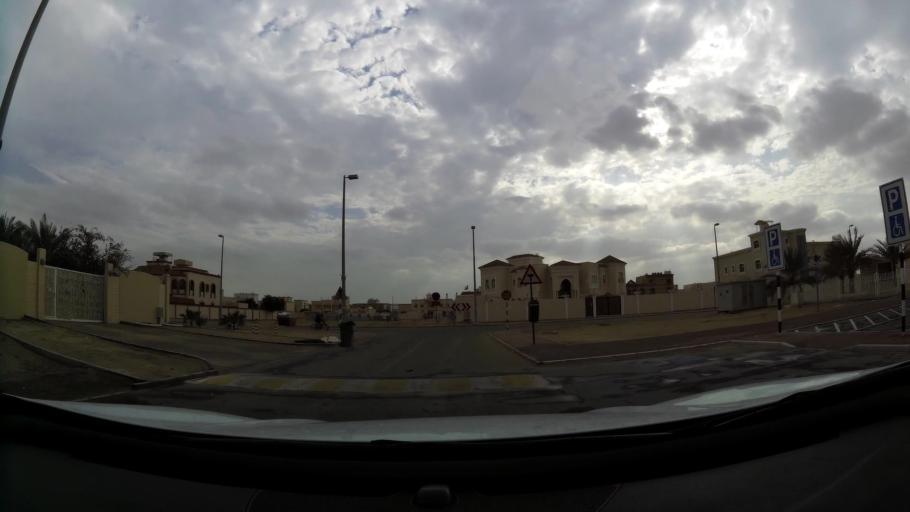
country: AE
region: Abu Dhabi
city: Abu Dhabi
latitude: 24.3396
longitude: 54.6264
